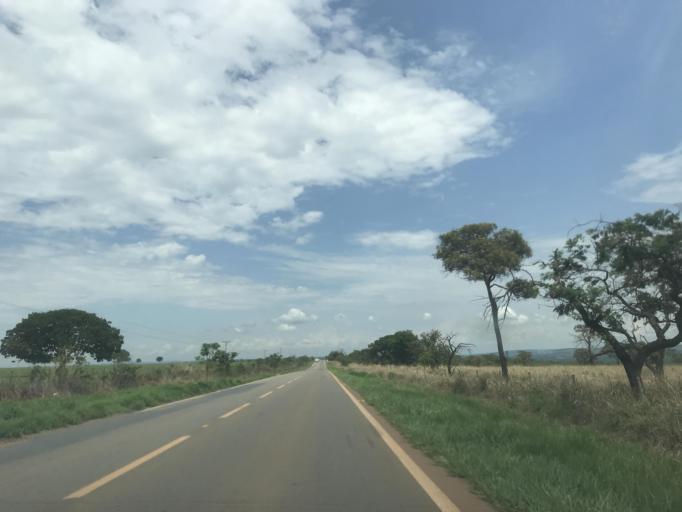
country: BR
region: Goias
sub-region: Luziania
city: Luziania
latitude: -16.3484
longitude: -48.0300
